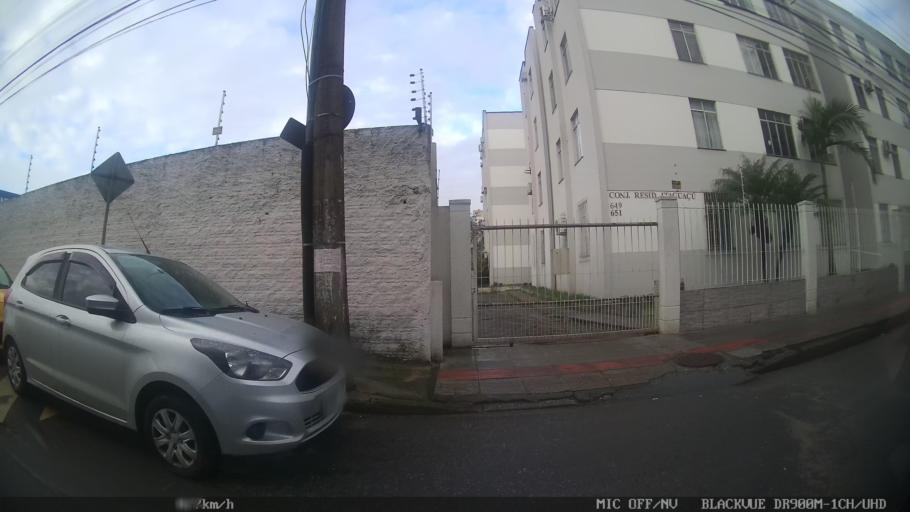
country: BR
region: Santa Catarina
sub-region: Sao Jose
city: Campinas
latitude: -27.5880
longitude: -48.6112
